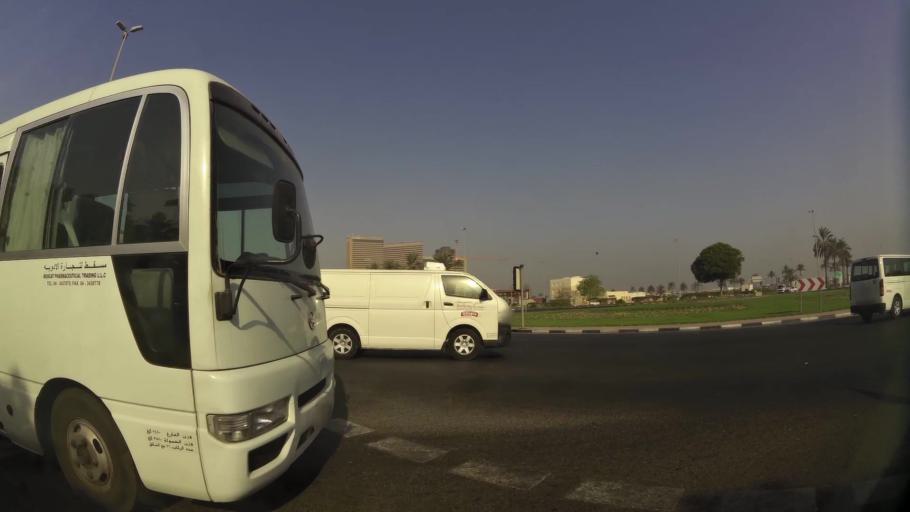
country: AE
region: Ash Shariqah
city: Sharjah
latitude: 25.2797
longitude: 55.3105
